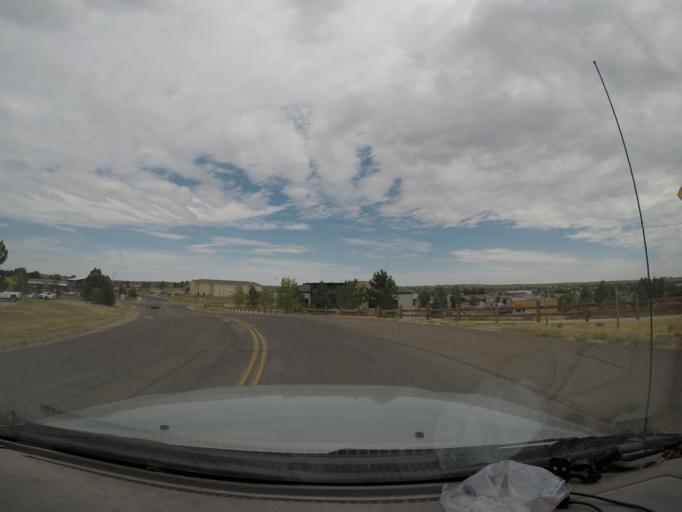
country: US
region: Wyoming
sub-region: Laramie County
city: Fox Farm-College
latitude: 41.1420
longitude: -104.7562
